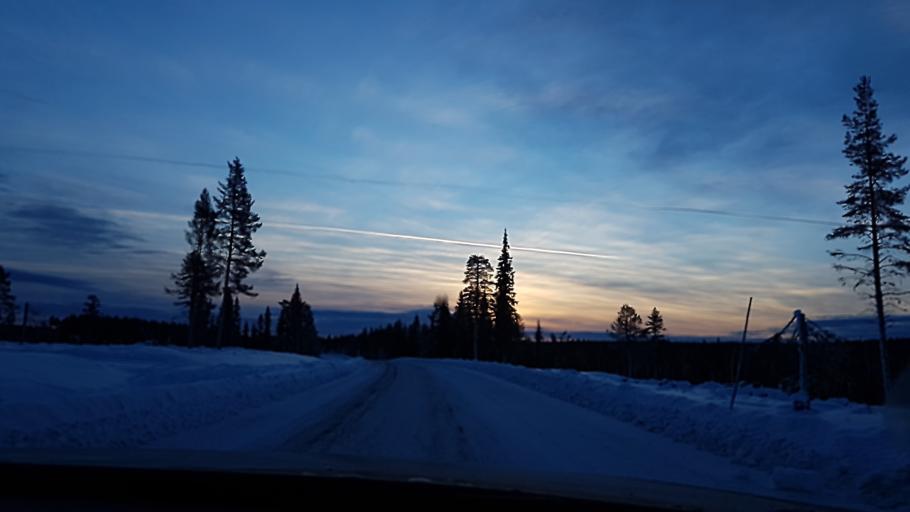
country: SE
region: Norrbotten
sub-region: Jokkmokks Kommun
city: Jokkmokk
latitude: 66.1211
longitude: 20.0313
